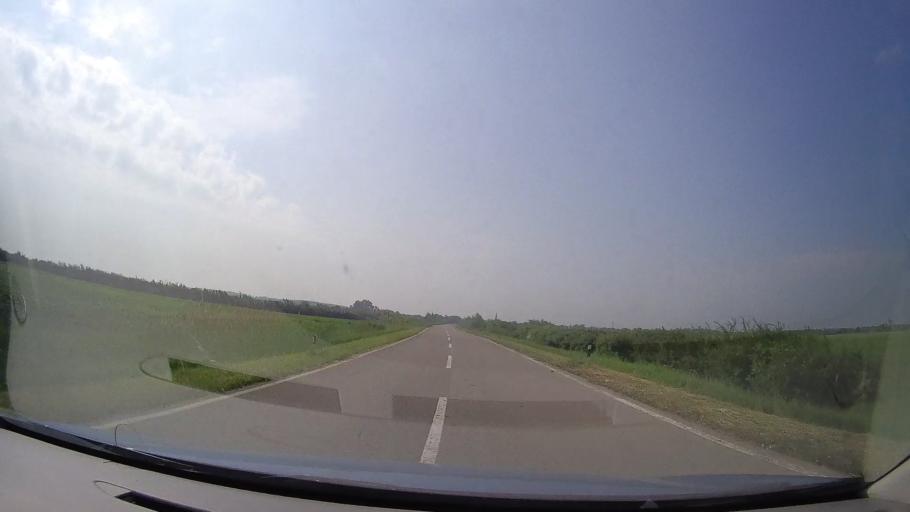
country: RS
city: Jasa Tomic
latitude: 45.4615
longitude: 20.8535
